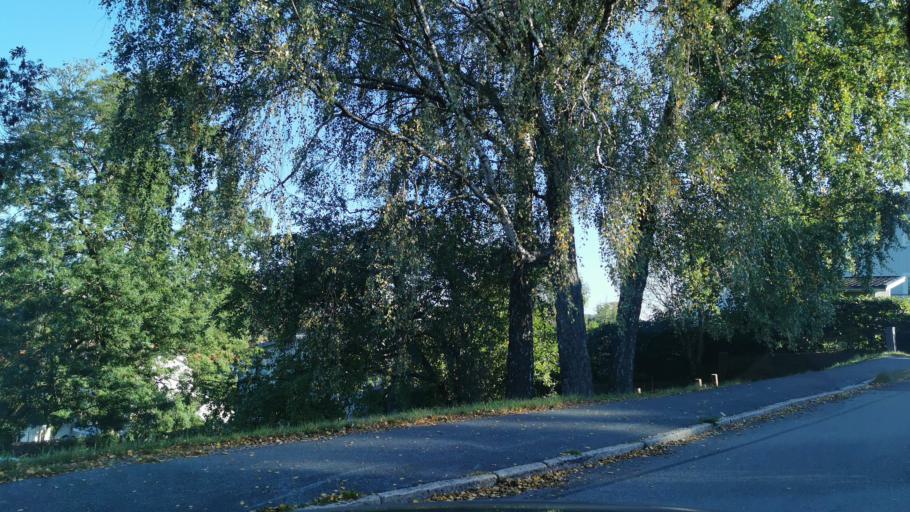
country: SE
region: Vaestra Goetaland
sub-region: Goteborg
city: Eriksbo
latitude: 57.7271
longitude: 12.0443
